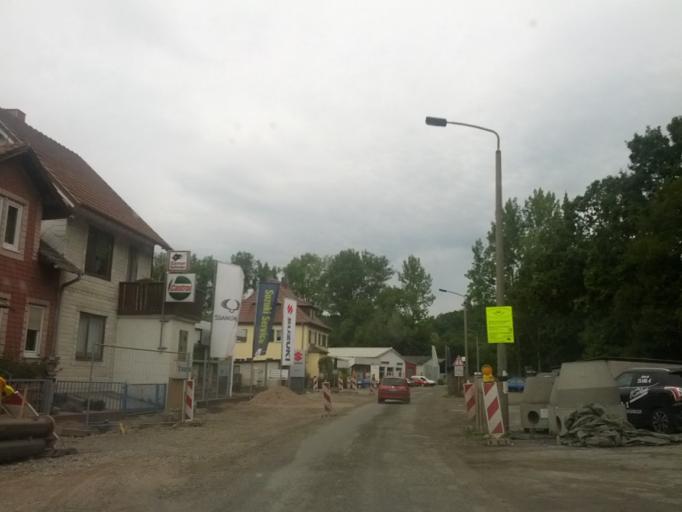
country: DE
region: Thuringia
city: Bad Salzungen
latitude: 50.8157
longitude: 10.2250
